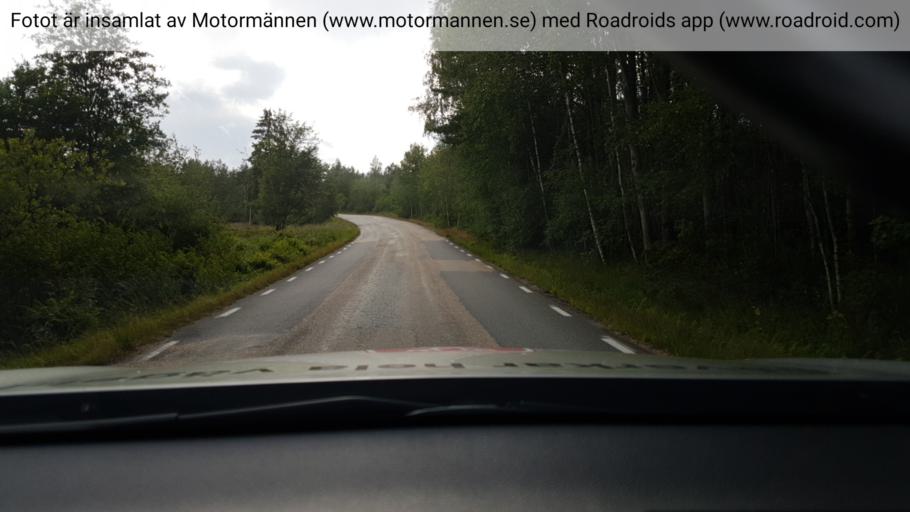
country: SE
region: Vaestra Goetaland
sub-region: Orust
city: Henan
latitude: 58.1610
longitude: 11.6852
